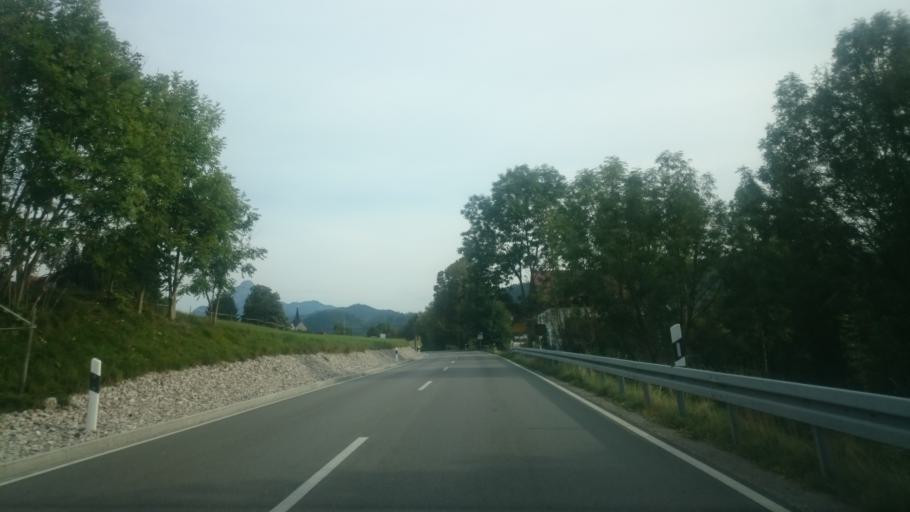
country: AT
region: Tyrol
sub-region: Politischer Bezirk Reutte
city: Vils
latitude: 47.5749
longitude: 10.6354
